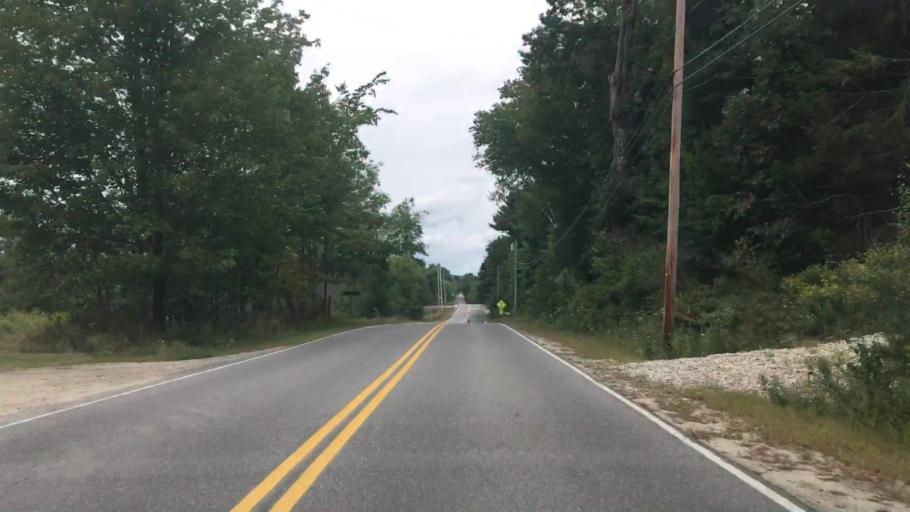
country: US
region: Maine
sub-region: Cumberland County
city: Yarmouth
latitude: 43.8579
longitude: -70.2168
